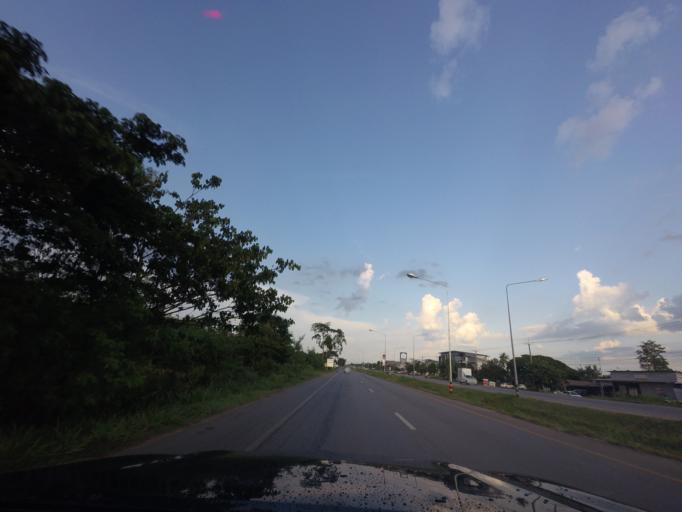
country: TH
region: Khon Kaen
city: Khon Kaen
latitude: 16.3990
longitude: 102.8659
